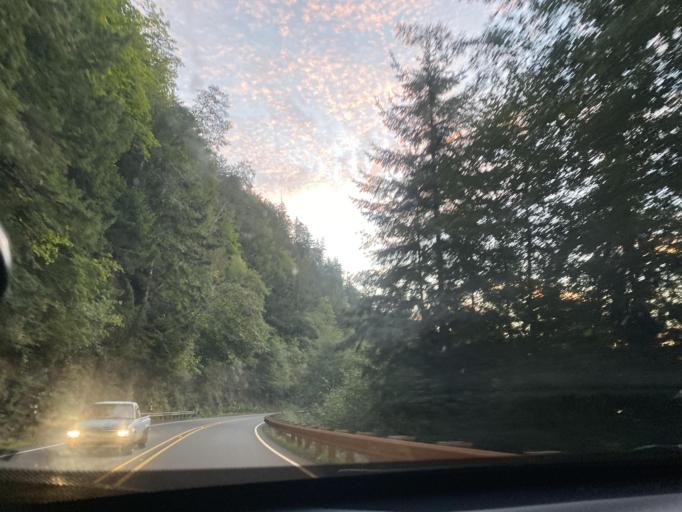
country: CA
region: British Columbia
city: Sooke
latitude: 48.0794
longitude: -123.7439
